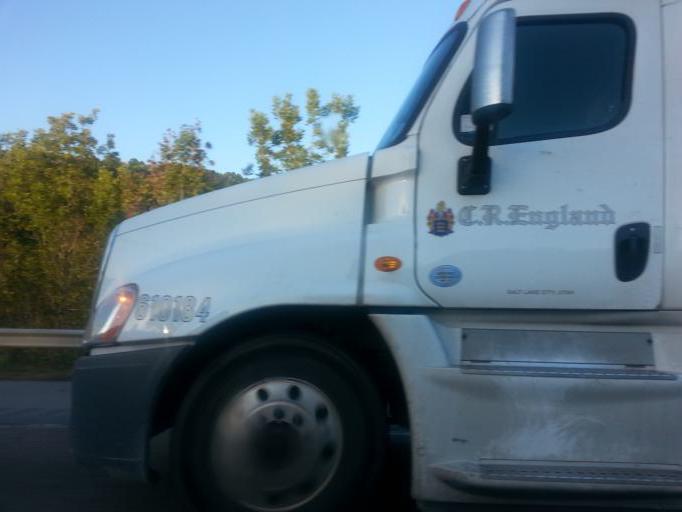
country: US
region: Tennessee
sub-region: Anderson County
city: Rocky Top
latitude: 36.2150
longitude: -84.1420
